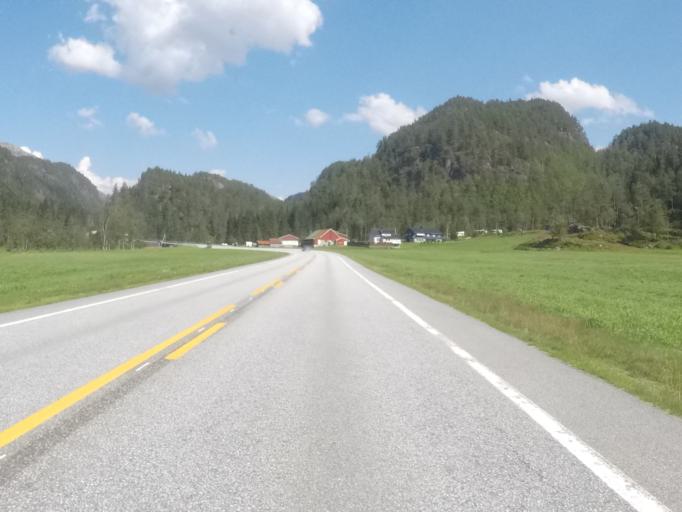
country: NO
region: Hordaland
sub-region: Modalen
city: Mo
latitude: 60.7516
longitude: 5.6279
